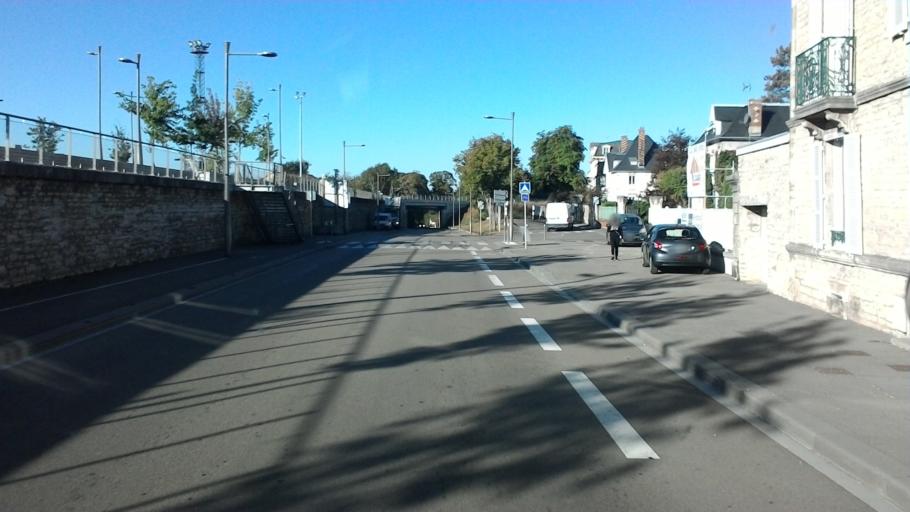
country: FR
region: Champagne-Ardenne
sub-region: Departement de la Haute-Marne
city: Chaumont
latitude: 48.1106
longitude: 5.1316
